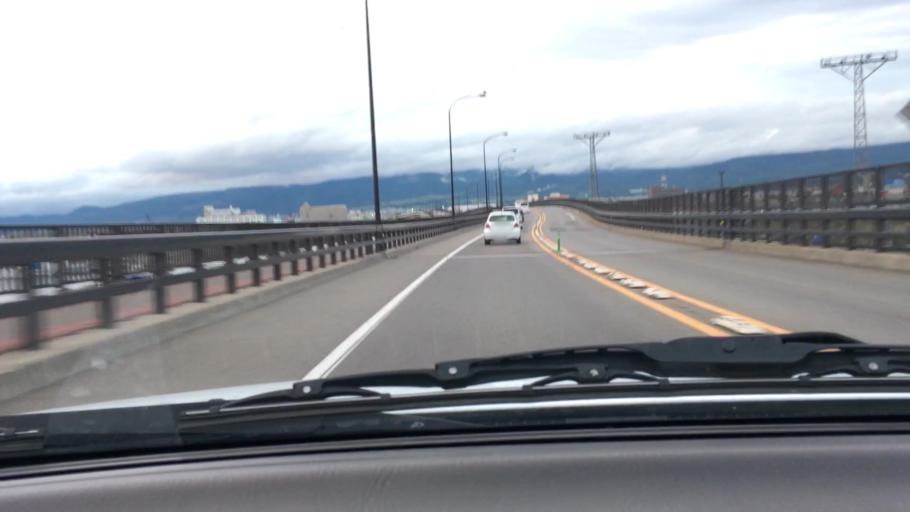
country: JP
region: Hokkaido
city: Hakodate
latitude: 41.7744
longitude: 140.7247
